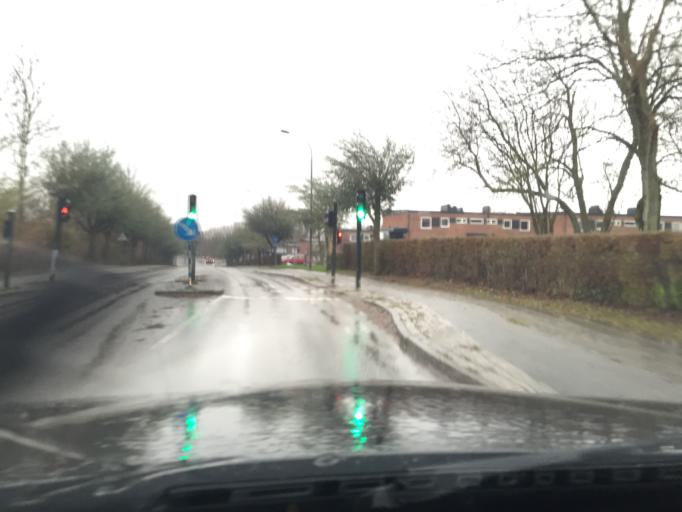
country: SE
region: Skane
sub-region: Lunds Kommun
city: Lund
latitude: 55.7028
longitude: 13.2302
